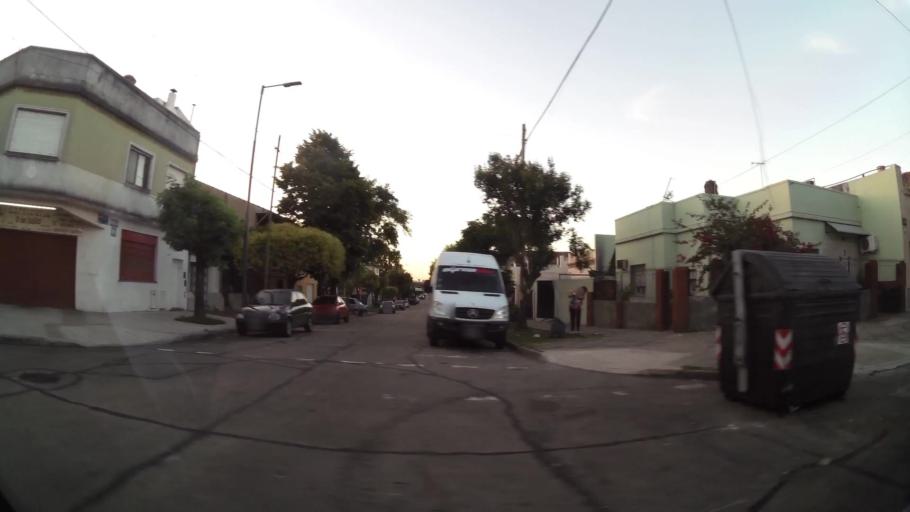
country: AR
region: Buenos Aires F.D.
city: Villa Lugano
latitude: -34.6705
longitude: -58.4724
